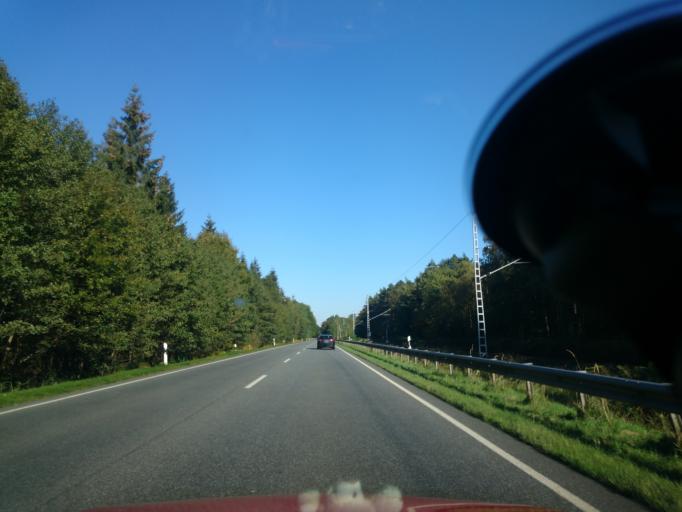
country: DE
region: Mecklenburg-Vorpommern
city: Gelbensande
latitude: 54.2142
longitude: 12.3437
